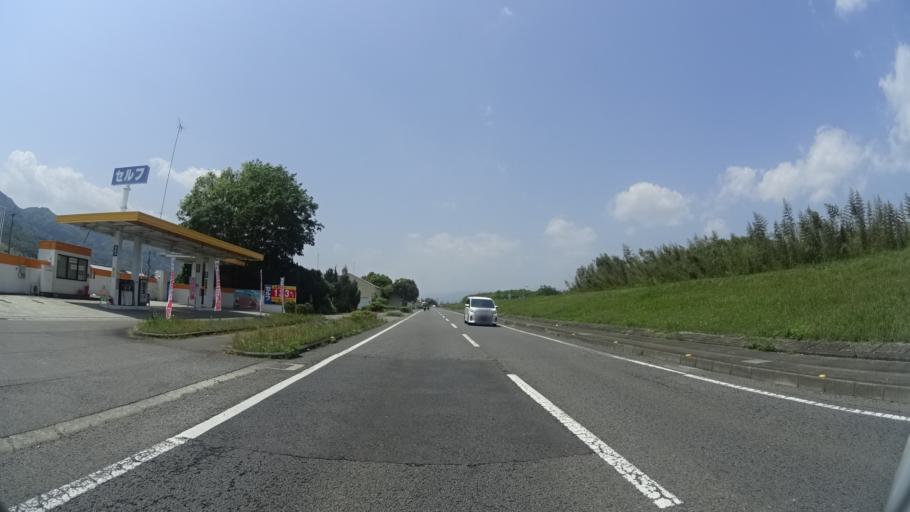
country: JP
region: Tokushima
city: Kamojimacho-jogejima
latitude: 34.0607
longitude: 134.3000
